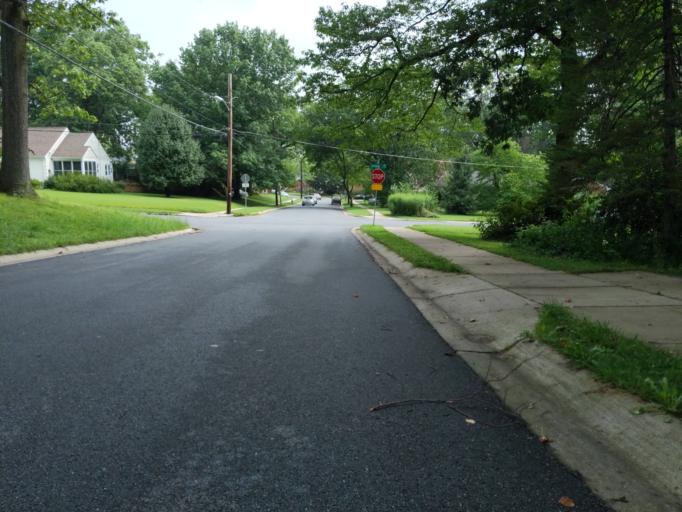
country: US
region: Maryland
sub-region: Montgomery County
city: Wheaton
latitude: 39.0304
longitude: -77.0546
